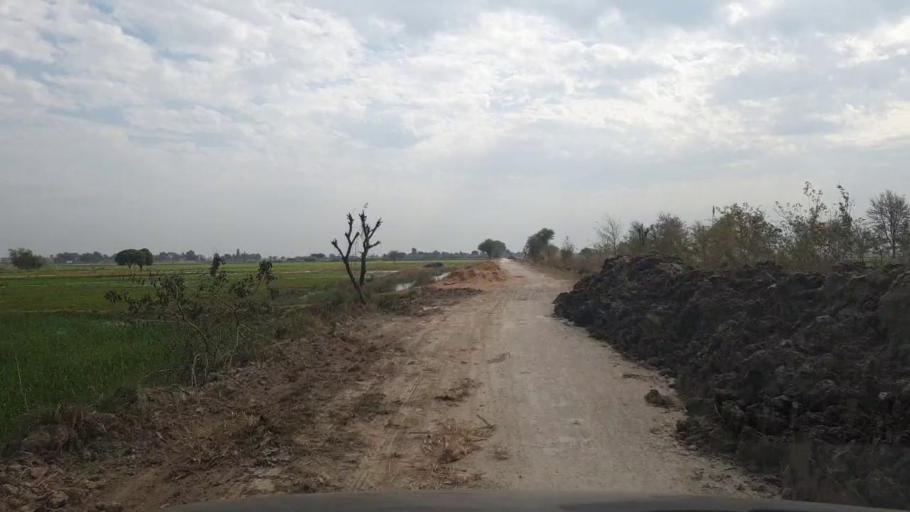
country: PK
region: Sindh
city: Hala
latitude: 26.0130
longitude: 68.4319
